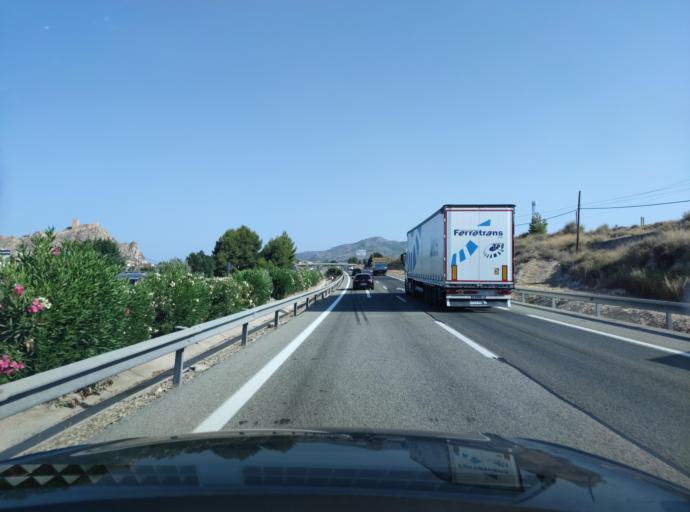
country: ES
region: Valencia
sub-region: Provincia de Alicante
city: Sax
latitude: 38.5327
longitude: -0.8080
